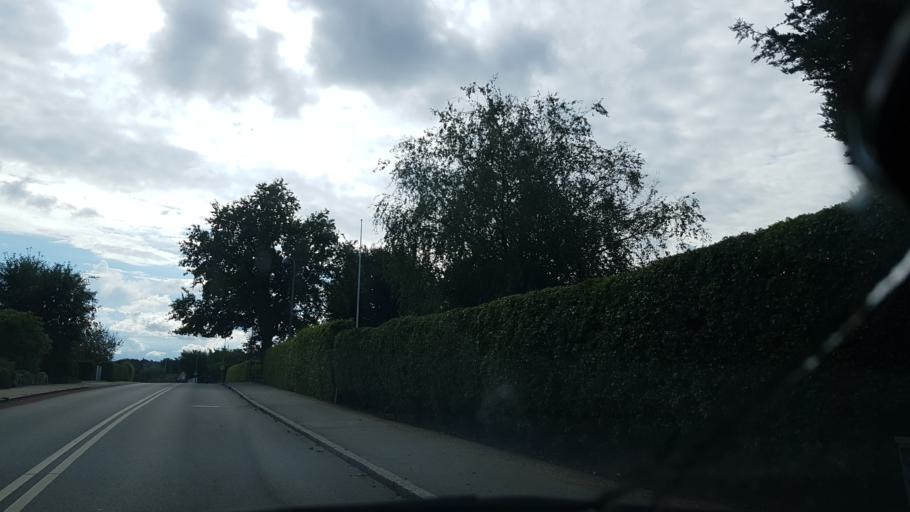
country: DK
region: Capital Region
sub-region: Helsingor Kommune
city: Espergaerde
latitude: 55.9908
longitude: 12.5427
